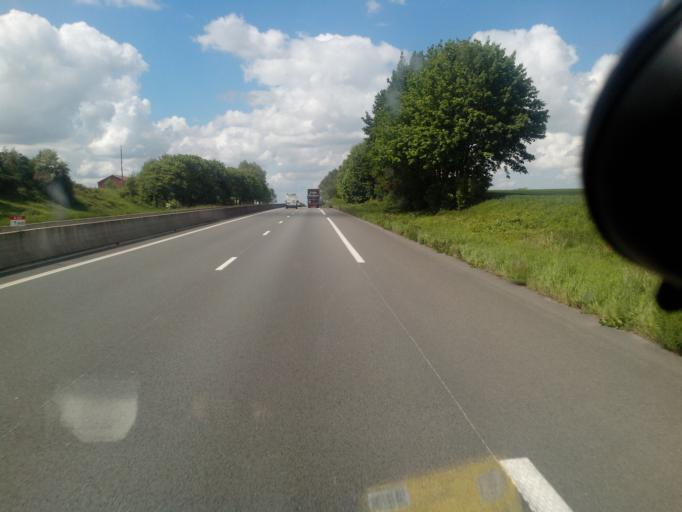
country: FR
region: Nord-Pas-de-Calais
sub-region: Departement du Nord
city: Godewaersvelde
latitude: 50.7661
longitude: 2.6385
